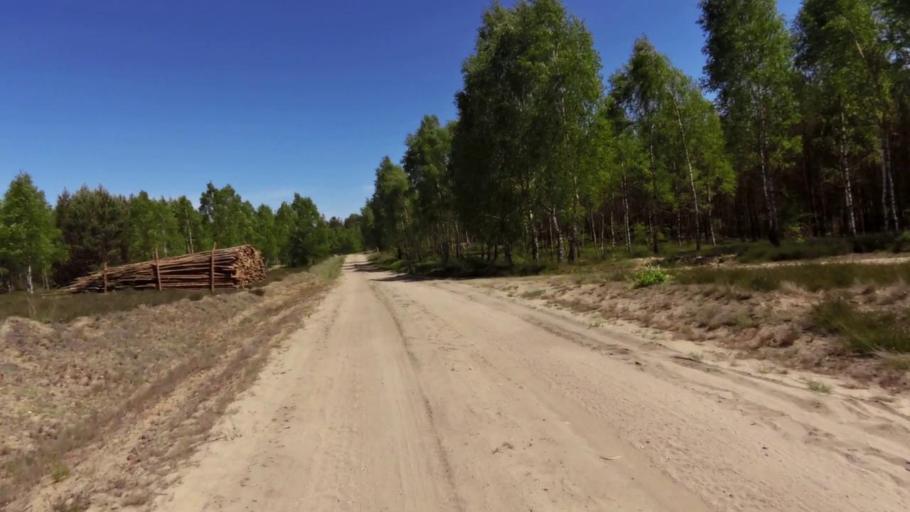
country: PL
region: West Pomeranian Voivodeship
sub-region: Powiat szczecinecki
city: Borne Sulinowo
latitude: 53.5749
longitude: 16.6384
